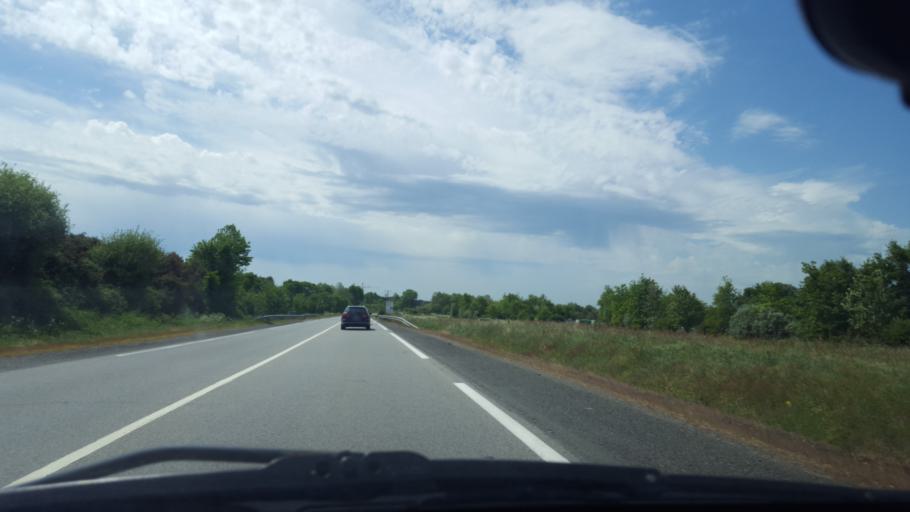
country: FR
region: Pays de la Loire
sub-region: Departement de la Loire-Atlantique
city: Paulx
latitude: 46.9962
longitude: -1.7462
